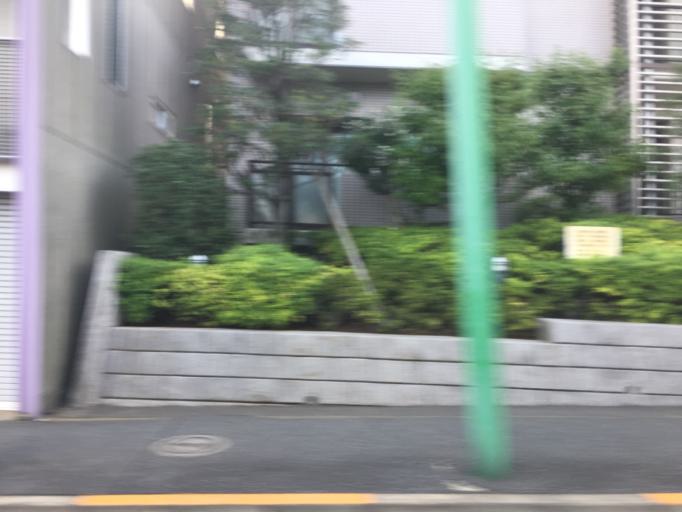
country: JP
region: Tokyo
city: Tokyo
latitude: 35.6118
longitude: 139.6478
